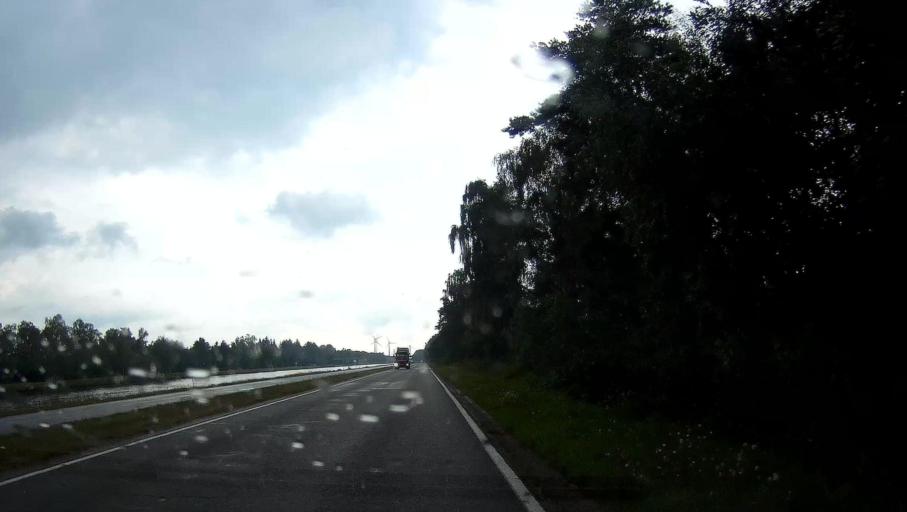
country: BE
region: Flanders
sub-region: Provincie Antwerpen
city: Dessel
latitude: 51.2290
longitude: 5.1632
